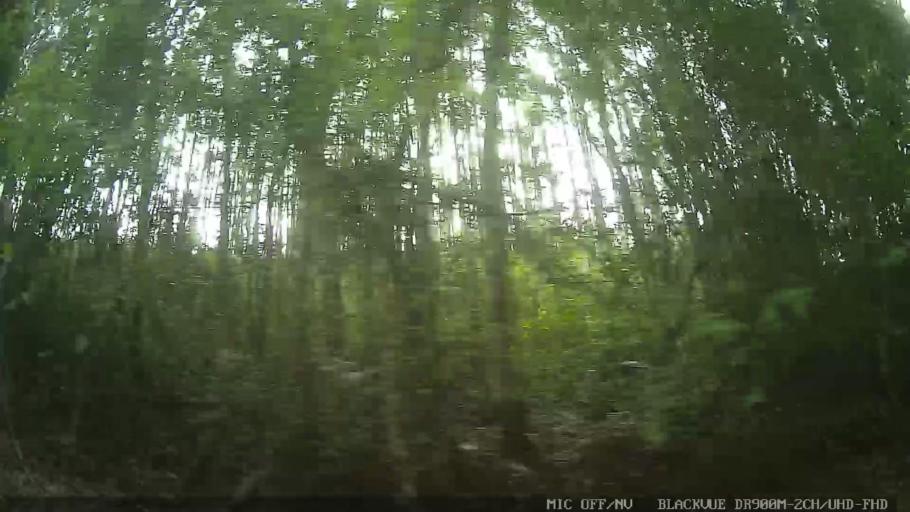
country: BR
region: Sao Paulo
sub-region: Santa Branca
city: Santa Branca
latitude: -23.5270
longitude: -45.7235
